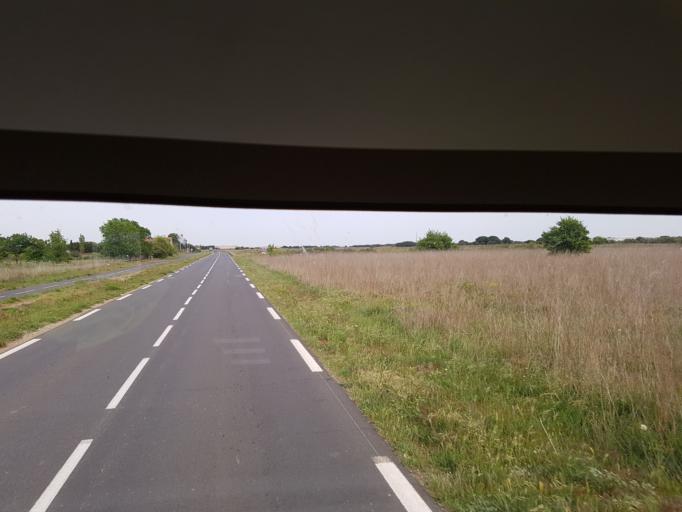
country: FR
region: Languedoc-Roussillon
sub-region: Departement de l'Herault
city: Sauvian
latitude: 43.2707
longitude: 3.2495
